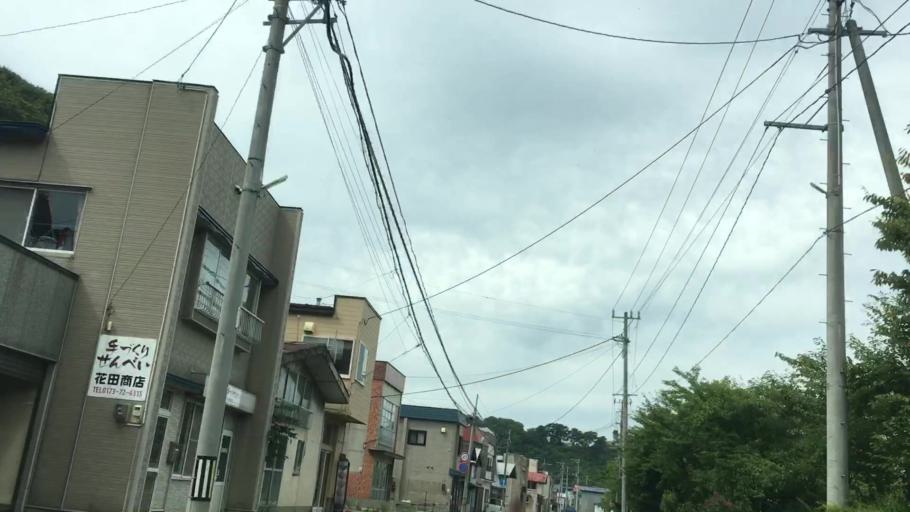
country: JP
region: Aomori
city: Shimokizukuri
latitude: 40.7783
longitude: 140.2121
